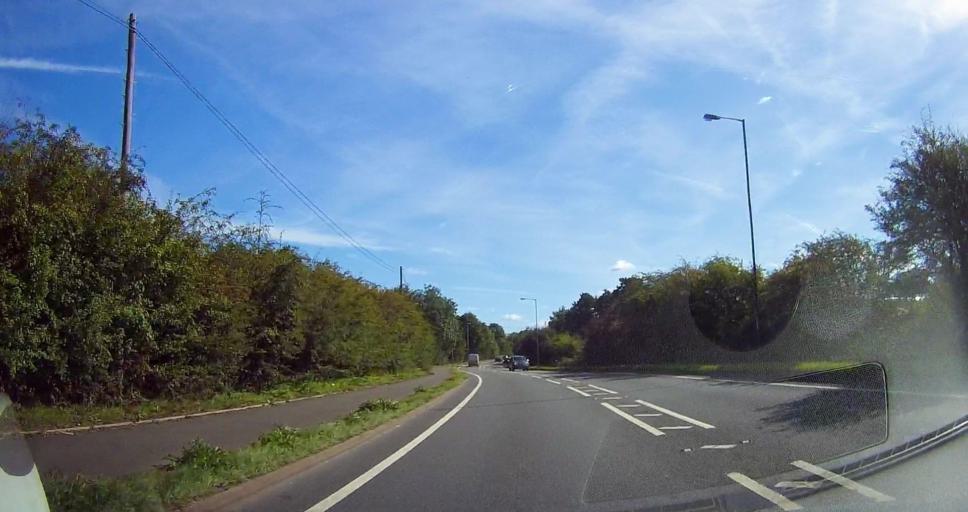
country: GB
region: England
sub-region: Staffordshire
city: Great Wyrley
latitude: 52.6702
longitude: -2.0139
